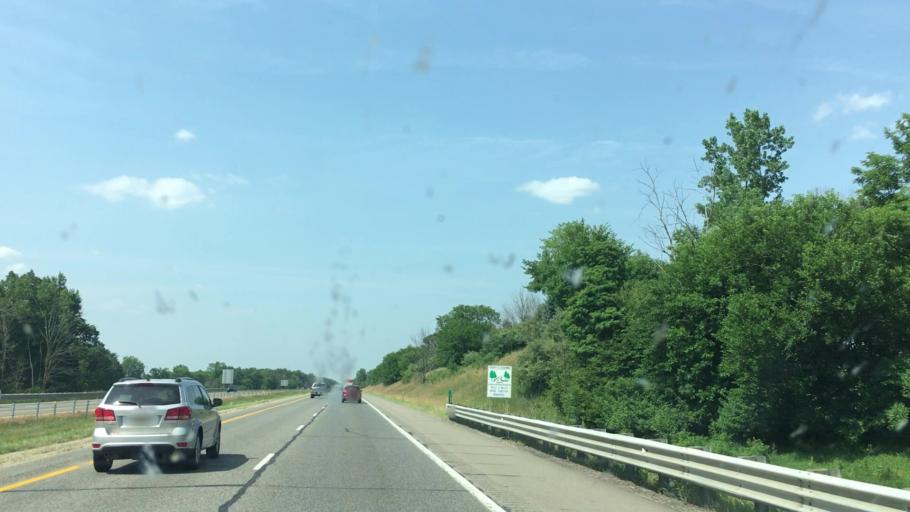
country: US
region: Michigan
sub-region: Allegan County
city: Otsego
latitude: 42.5522
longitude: -85.6620
